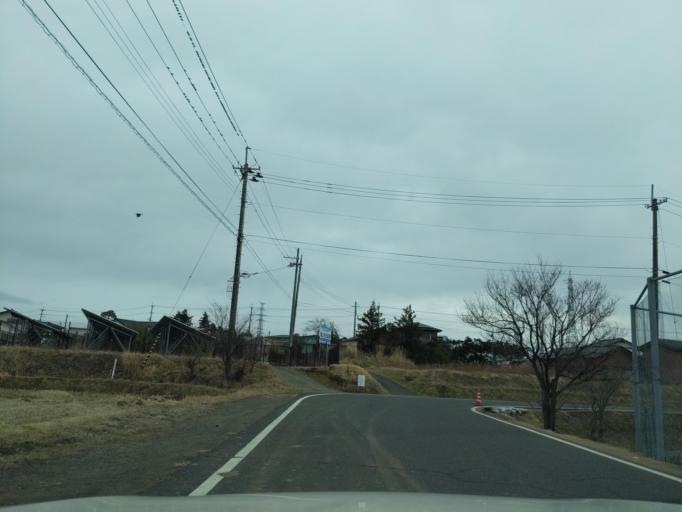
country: JP
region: Fukushima
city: Koriyama
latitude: 37.4549
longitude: 140.3843
